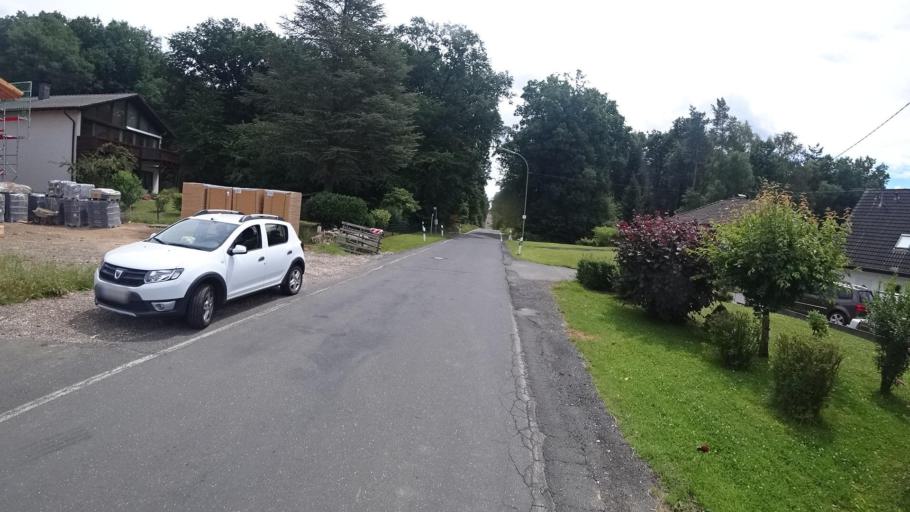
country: DE
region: Rheinland-Pfalz
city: Kircheib
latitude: 50.7063
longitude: 7.4709
